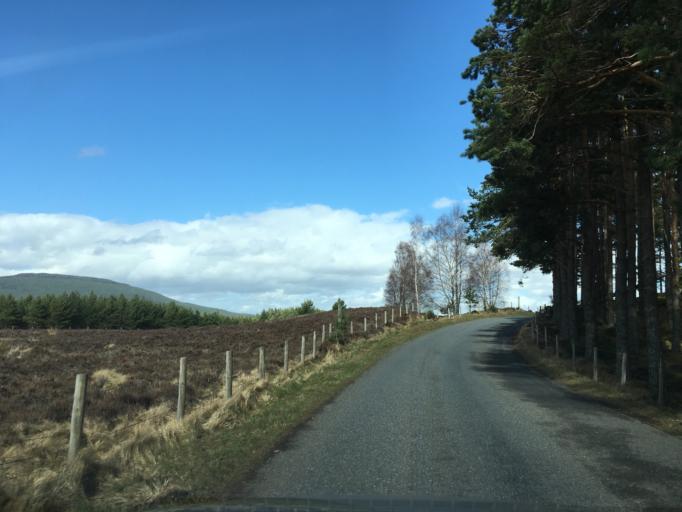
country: GB
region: Scotland
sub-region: Highland
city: Aviemore
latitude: 57.2003
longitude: -3.7983
